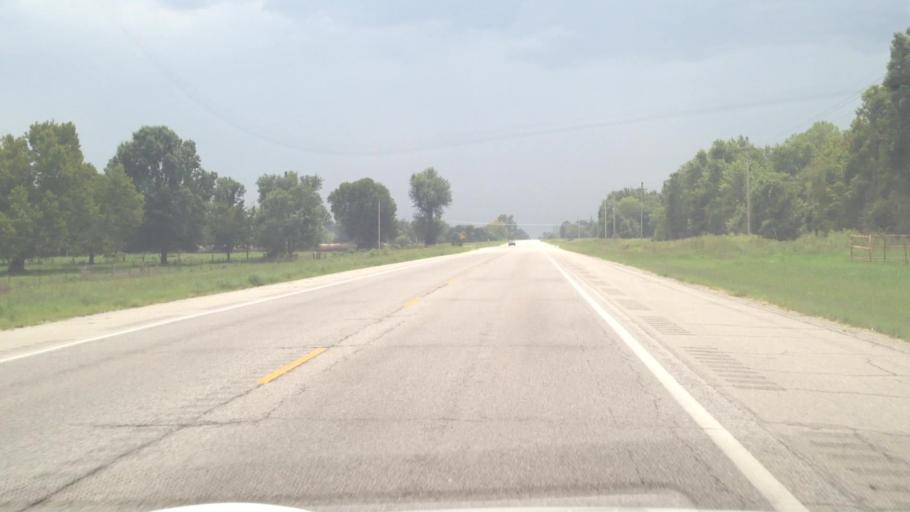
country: US
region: Kansas
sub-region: Cherokee County
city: Galena
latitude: 37.1246
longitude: -94.7044
